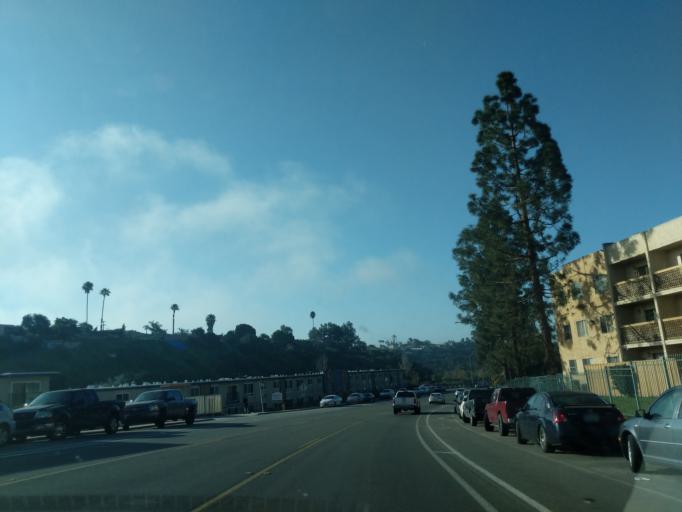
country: US
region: California
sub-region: San Diego County
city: National City
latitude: 32.7365
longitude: -117.0924
